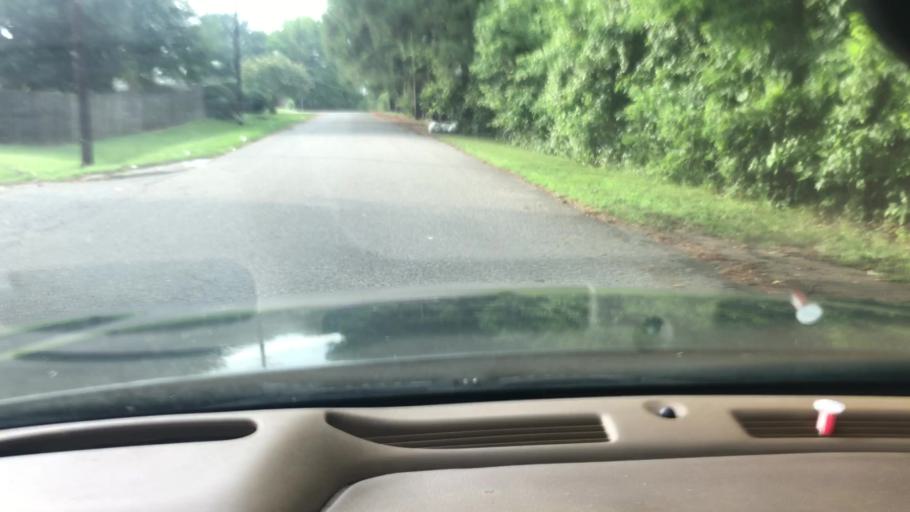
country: US
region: Mississippi
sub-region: De Soto County
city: Southaven
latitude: 35.0459
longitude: -90.0084
